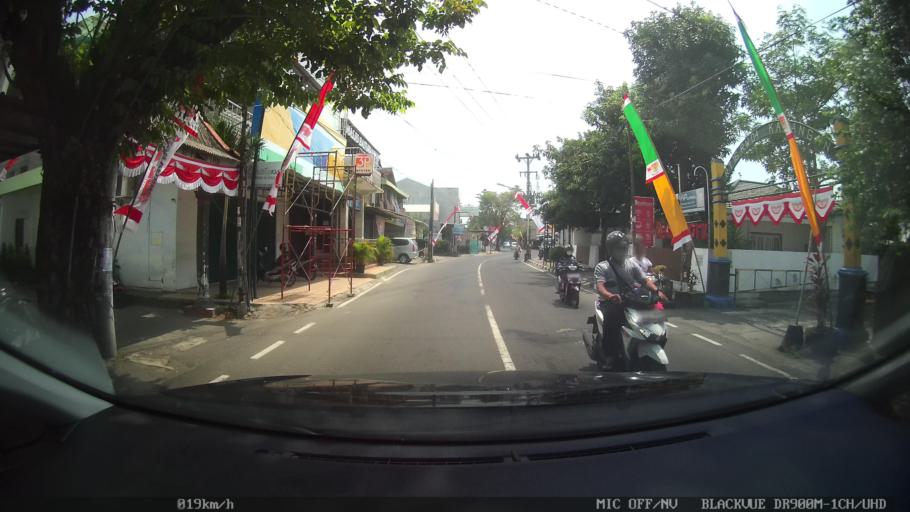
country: ID
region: Daerah Istimewa Yogyakarta
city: Yogyakarta
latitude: -7.8135
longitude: 110.3865
